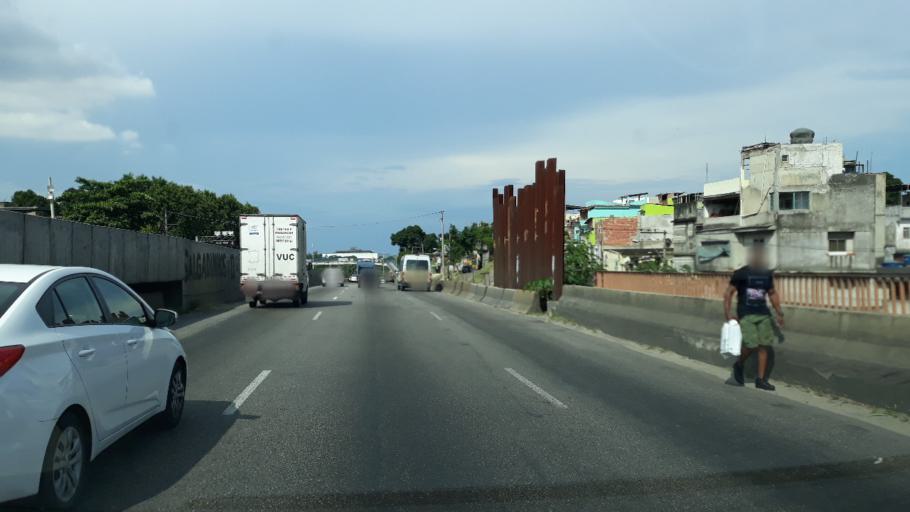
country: BR
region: Rio de Janeiro
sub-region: Sao Joao De Meriti
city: Sao Joao de Meriti
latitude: -22.8366
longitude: -43.3633
